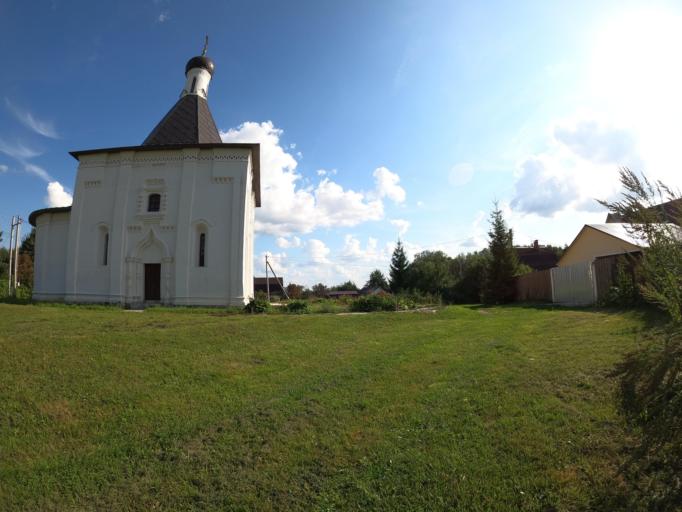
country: RU
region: Moskovskaya
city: Troitskoye
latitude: 55.2135
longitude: 38.4876
